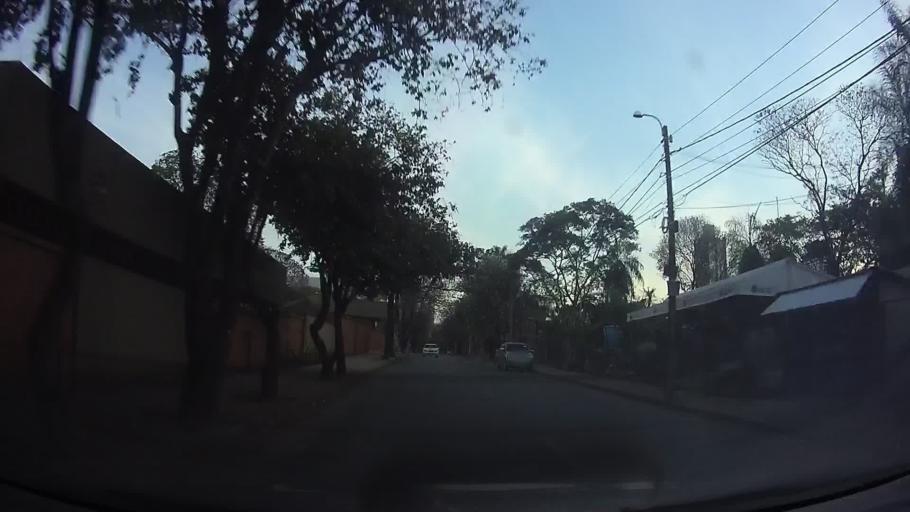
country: PY
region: Central
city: Fernando de la Mora
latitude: -25.2827
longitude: -57.5572
